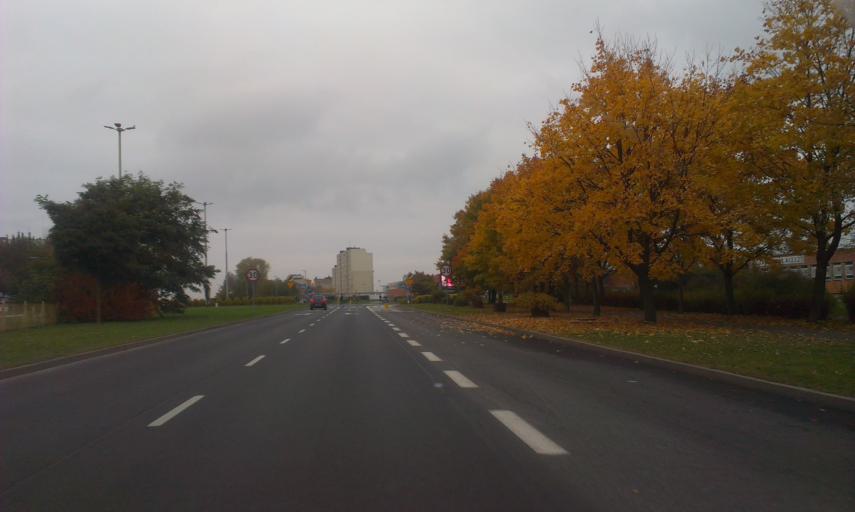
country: PL
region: West Pomeranian Voivodeship
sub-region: Koszalin
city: Koszalin
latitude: 54.2044
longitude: 16.1846
